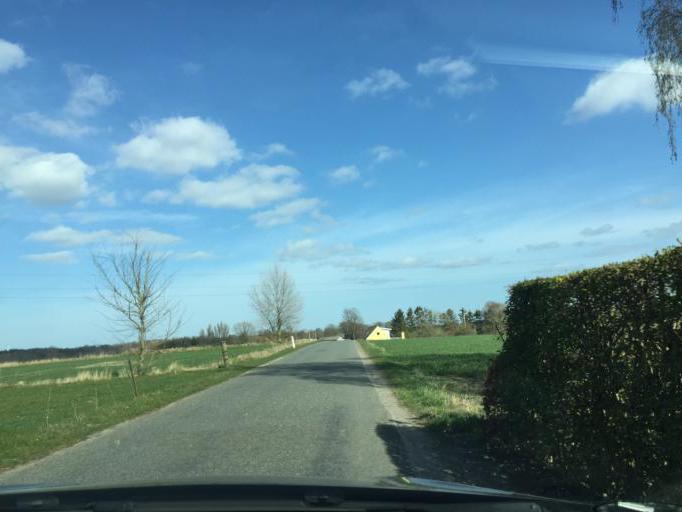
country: DK
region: South Denmark
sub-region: Faaborg-Midtfyn Kommune
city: Arslev
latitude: 55.2959
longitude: 10.5067
